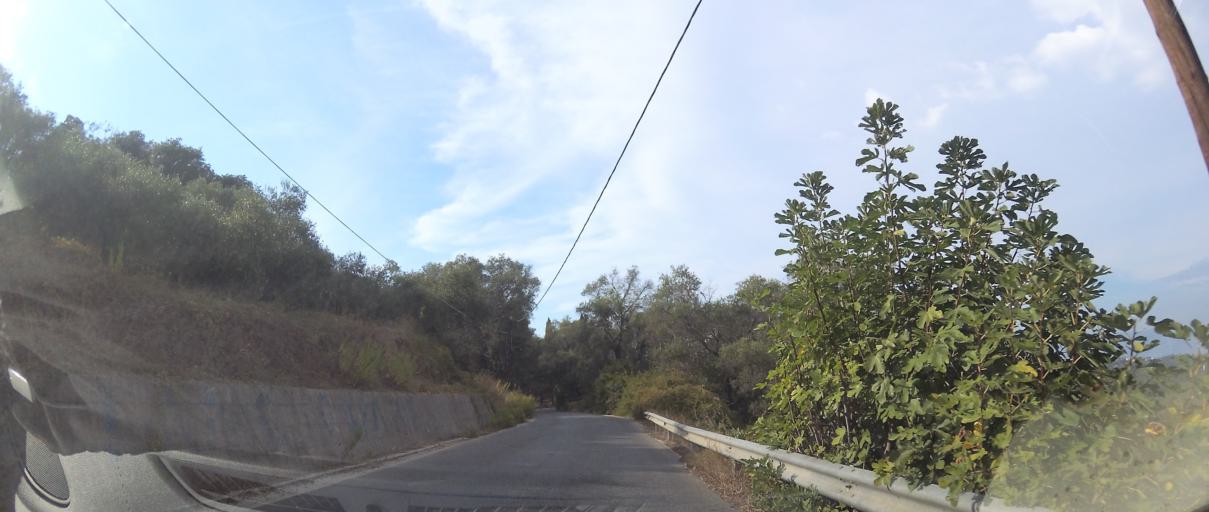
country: GR
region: Ionian Islands
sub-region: Nomos Kerkyras
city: Kynopiastes
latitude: 39.5550
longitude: 19.8598
